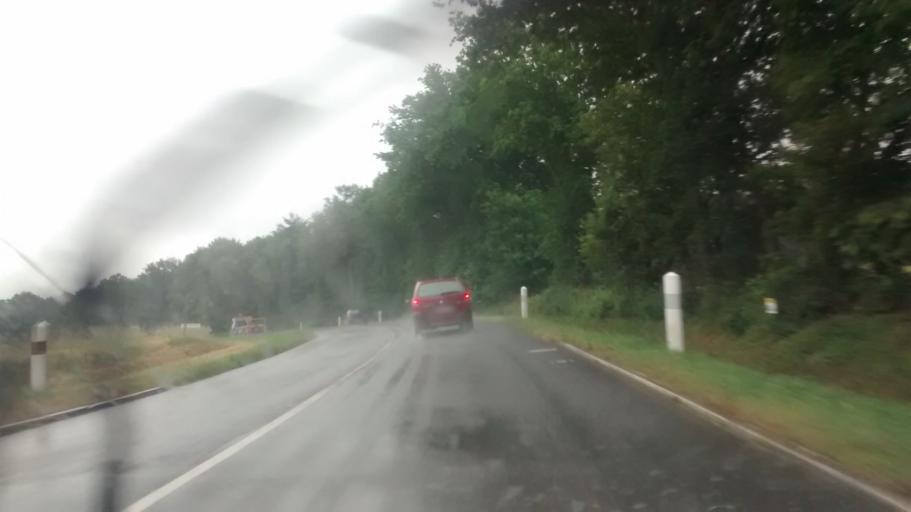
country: FR
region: Brittany
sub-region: Departement du Morbihan
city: Saint-Martin-sur-Oust
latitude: 47.7836
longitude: -2.2127
